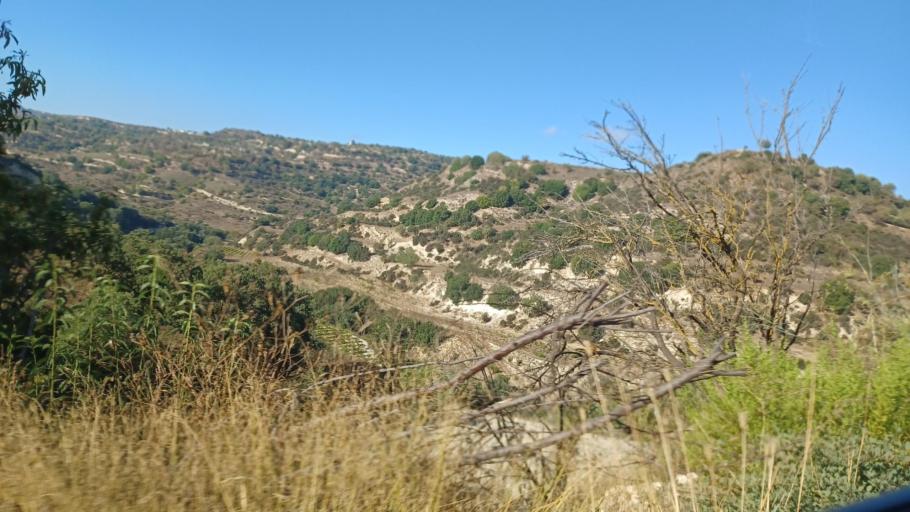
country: CY
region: Pafos
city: Mesogi
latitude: 34.8460
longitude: 32.5206
